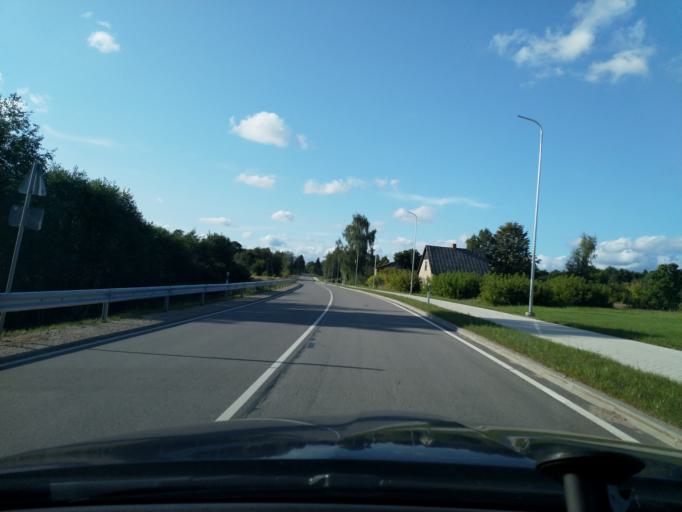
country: LV
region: Kuldigas Rajons
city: Kuldiga
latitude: 56.9668
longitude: 22.0027
